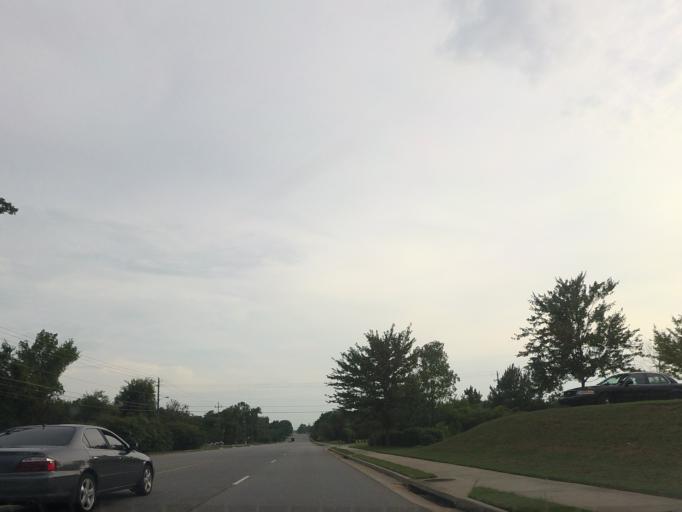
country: US
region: Georgia
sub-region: Houston County
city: Centerville
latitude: 32.7321
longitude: -83.6804
